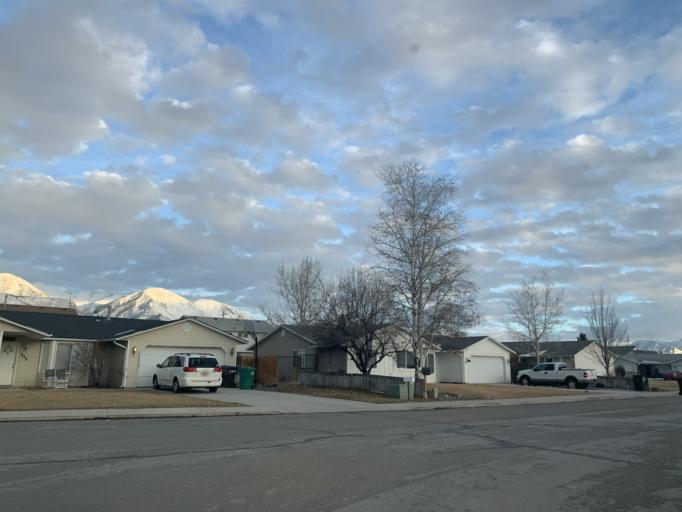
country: US
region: Utah
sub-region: Utah County
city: Orem
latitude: 40.2470
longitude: -111.7089
